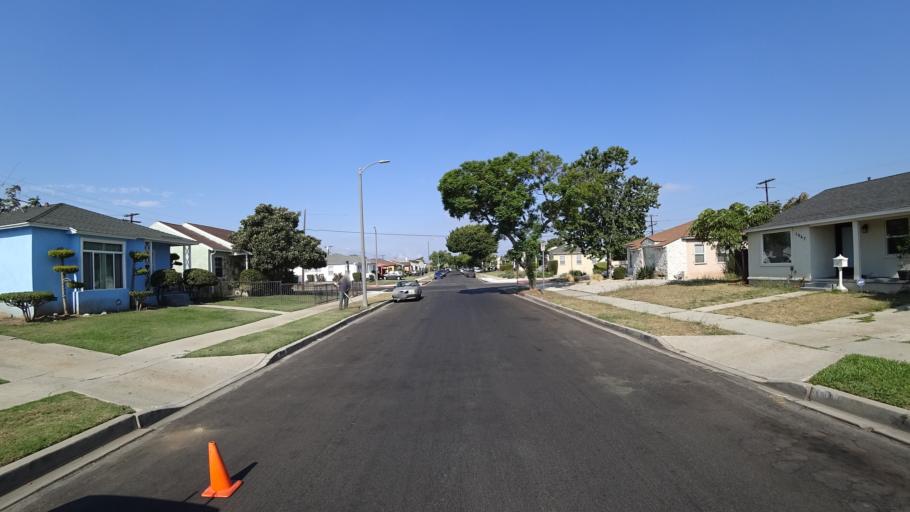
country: US
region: California
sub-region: Los Angeles County
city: Westmont
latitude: 33.9498
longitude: -118.3130
